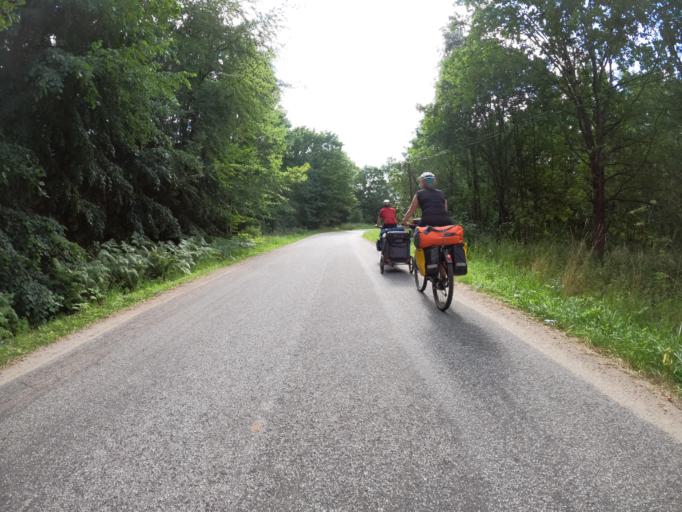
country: PL
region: West Pomeranian Voivodeship
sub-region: Powiat swidwinski
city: Swidwin
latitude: 53.7547
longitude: 15.6778
